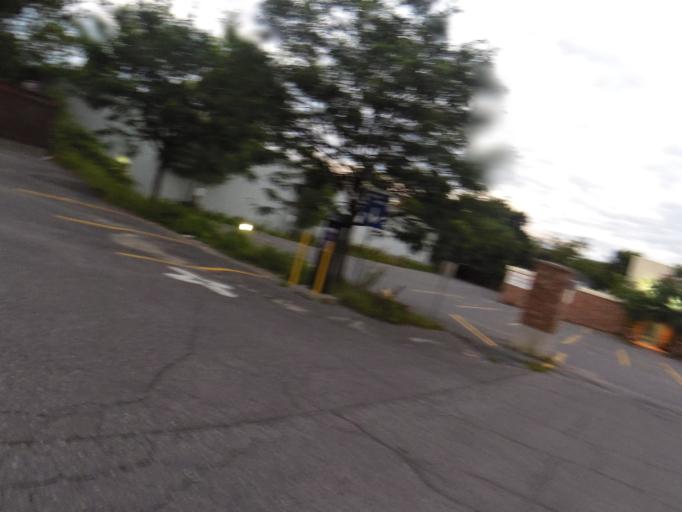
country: CA
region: Ontario
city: Ottawa
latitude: 45.3935
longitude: -75.7526
